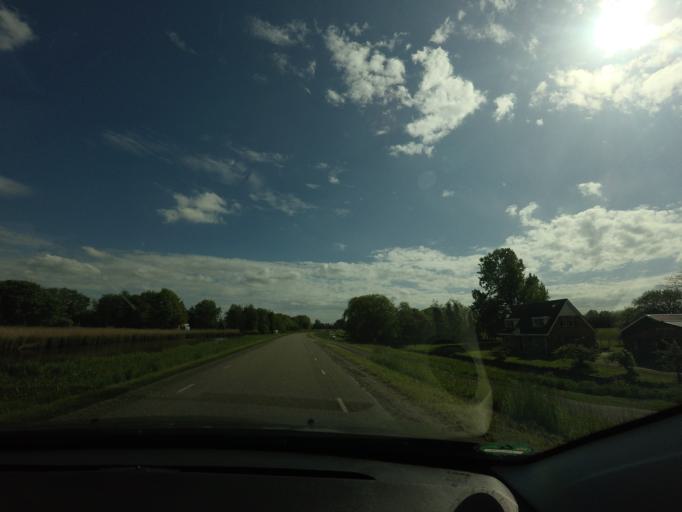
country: NL
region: North Holland
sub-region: Gemeente Heerhugowaard
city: Heerhugowaard
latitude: 52.6742
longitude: 4.8734
